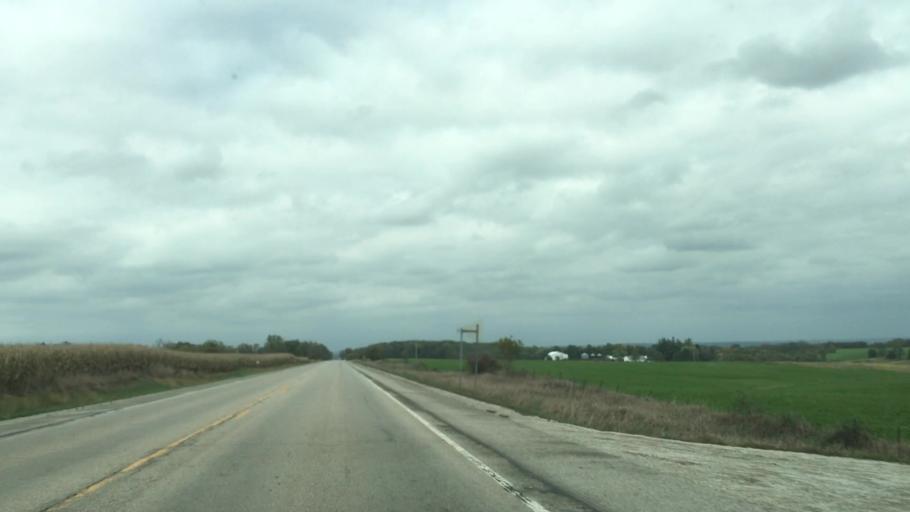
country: US
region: Minnesota
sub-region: Fillmore County
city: Preston
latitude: 43.7563
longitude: -92.1342
